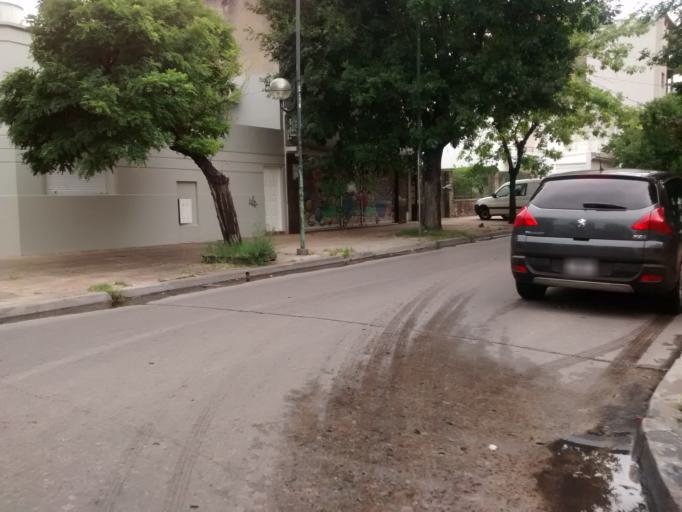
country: AR
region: Buenos Aires
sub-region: Partido de La Plata
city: La Plata
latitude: -34.9050
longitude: -57.9654
